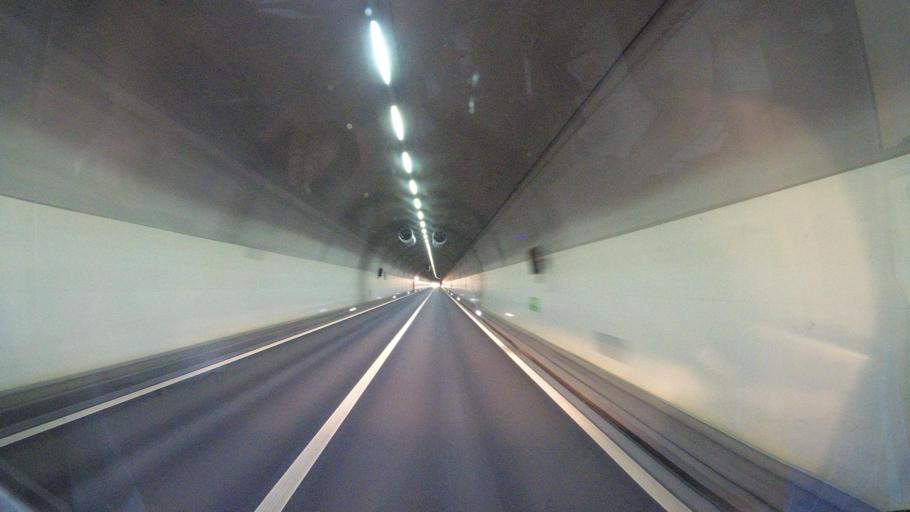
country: CH
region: Saint Gallen
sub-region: Wahlkreis Toggenburg
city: Wattwil
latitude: 47.2966
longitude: 9.0823
